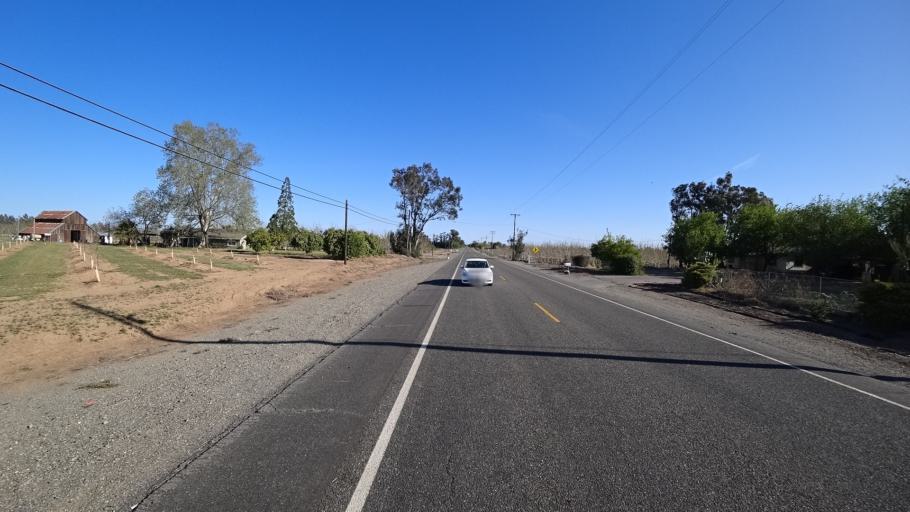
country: US
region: California
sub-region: Glenn County
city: Orland
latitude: 39.7854
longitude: -122.1977
